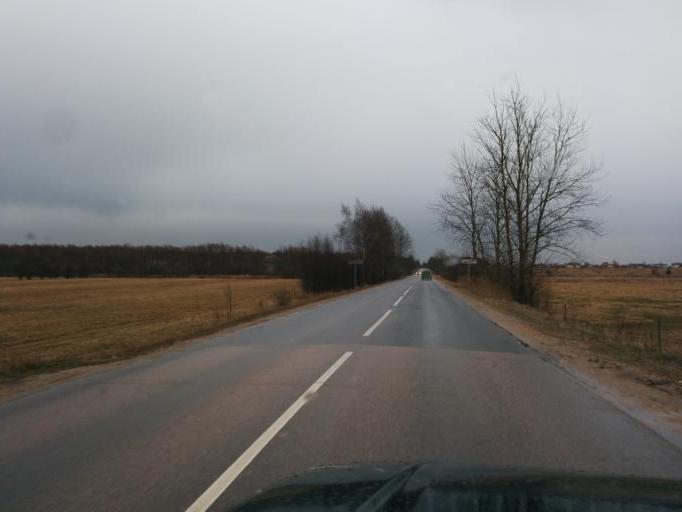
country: LV
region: Kekava
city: Balozi
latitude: 56.8944
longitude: 24.1551
